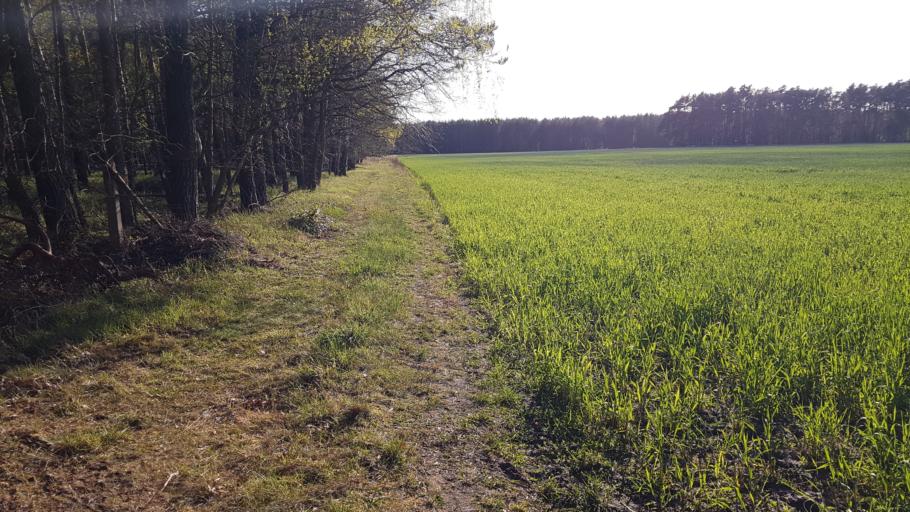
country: DE
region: Brandenburg
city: Schilda
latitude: 51.5942
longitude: 13.3550
